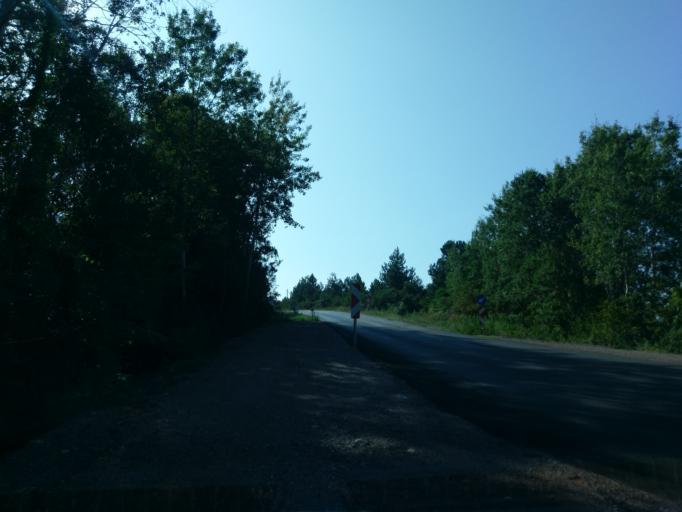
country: TR
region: Sinop
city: Yenikonak
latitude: 41.9433
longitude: 34.7311
